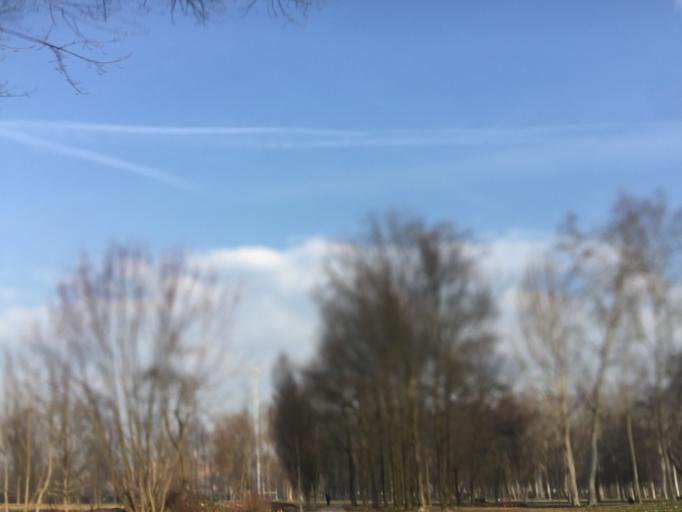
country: IT
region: Lombardy
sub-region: Citta metropolitana di Milano
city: Romano Banco
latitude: 45.4337
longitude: 9.1419
